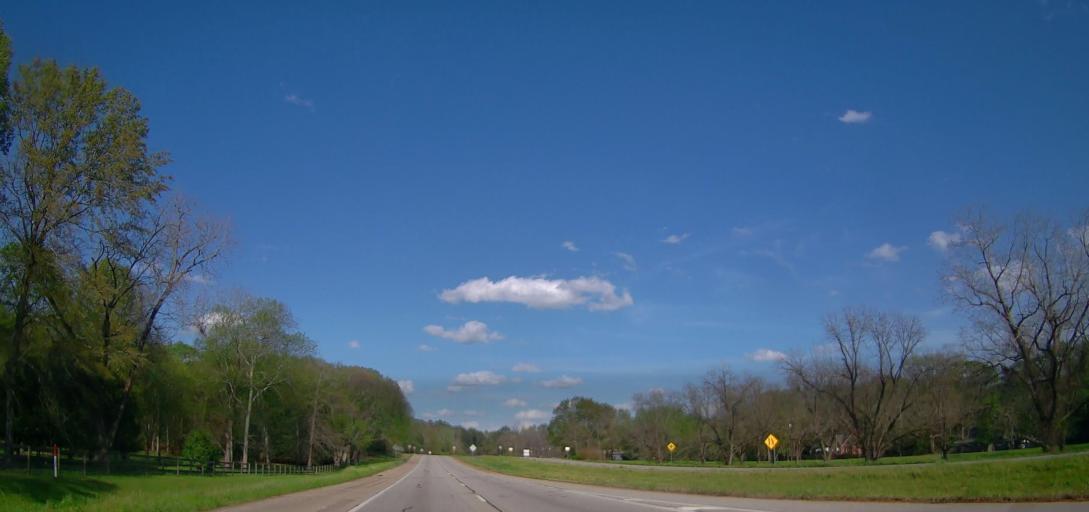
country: US
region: Georgia
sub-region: Baldwin County
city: Hardwick
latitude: 33.0852
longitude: -83.2092
